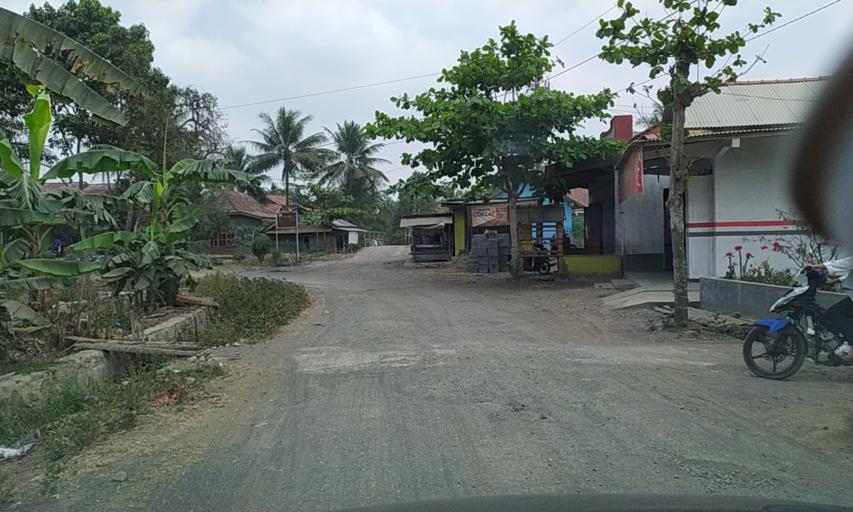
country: ID
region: Central Java
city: Sidakaya
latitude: -7.5673
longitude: 108.8667
